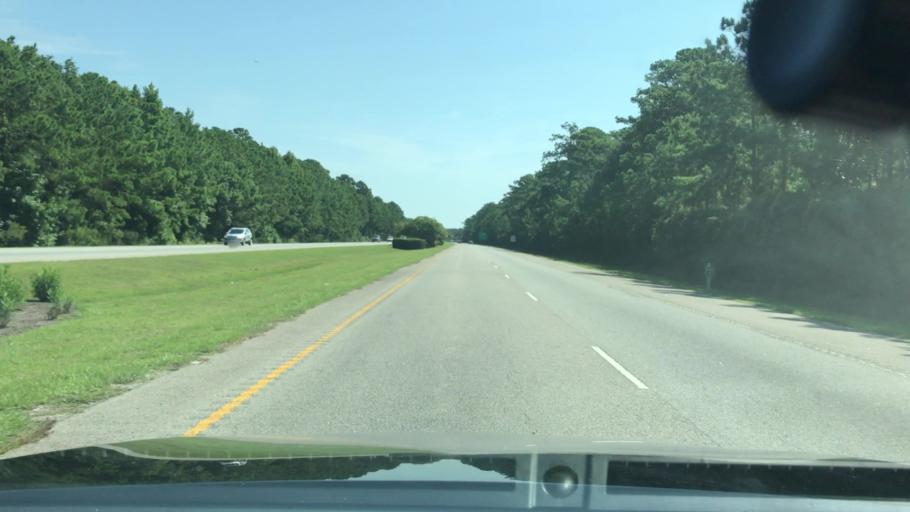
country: US
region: South Carolina
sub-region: Beaufort County
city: Hilton Head Island
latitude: 32.1993
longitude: -80.7556
